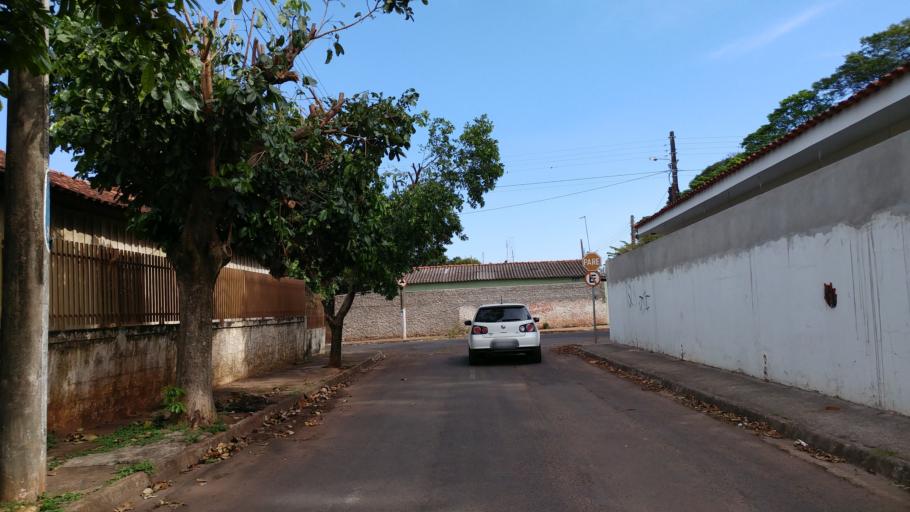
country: BR
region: Sao Paulo
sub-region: Paraguacu Paulista
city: Paraguacu Paulista
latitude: -22.4108
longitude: -50.5807
